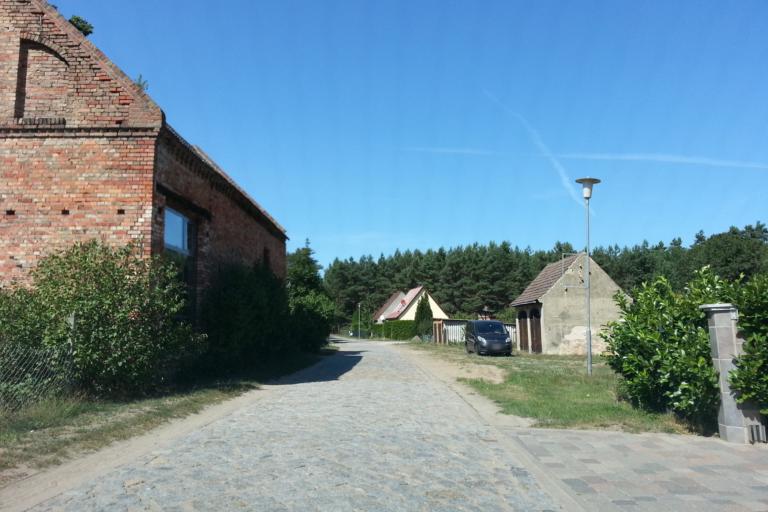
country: DE
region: Mecklenburg-Vorpommern
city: Jatznick
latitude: 53.6327
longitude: 13.9504
